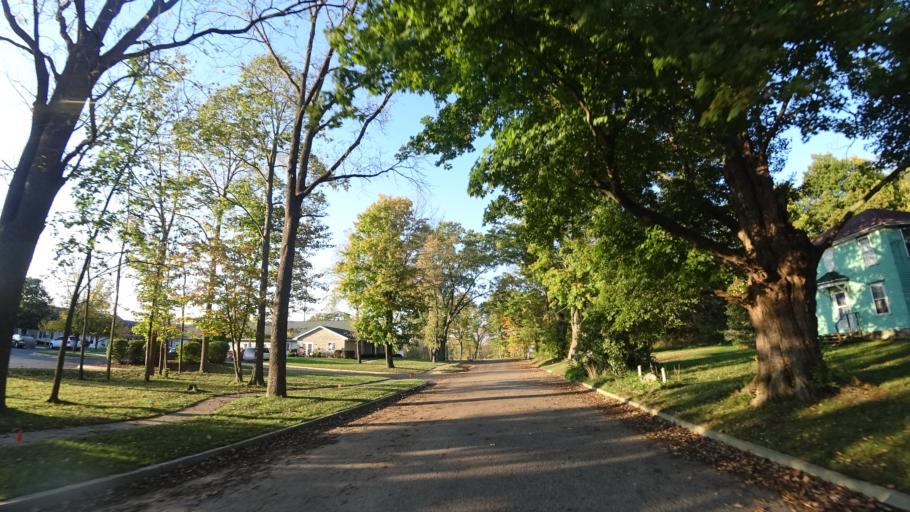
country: US
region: Michigan
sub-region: Saint Joseph County
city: Three Rivers
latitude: 41.9501
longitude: -85.6432
